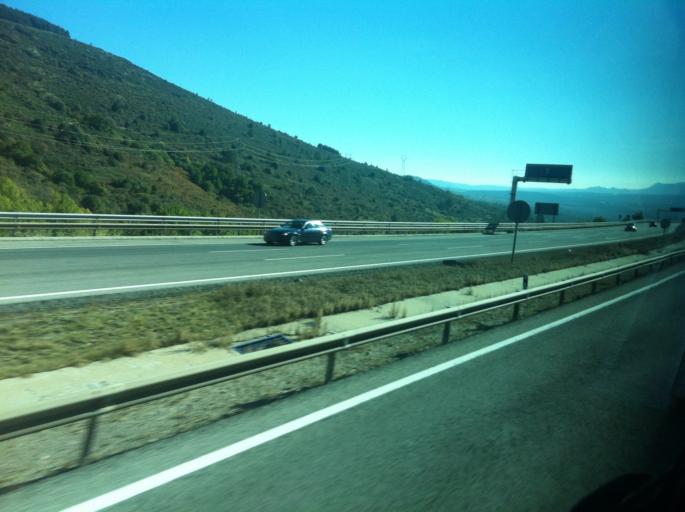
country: ES
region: Madrid
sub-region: Provincia de Madrid
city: Robregordo
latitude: 41.1176
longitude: -3.5867
